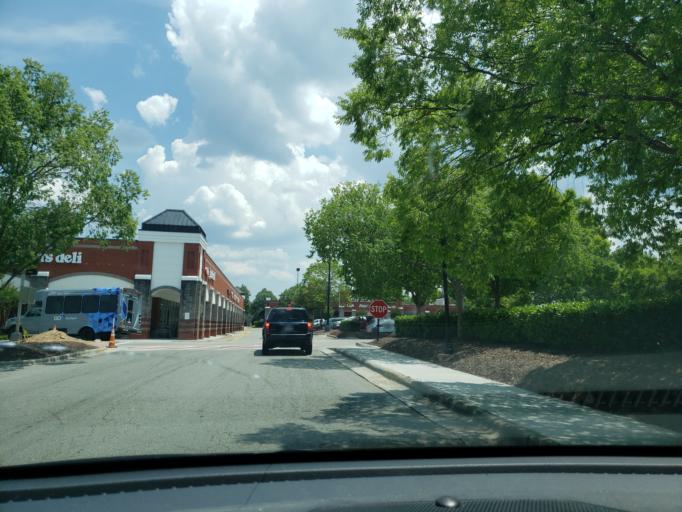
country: US
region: North Carolina
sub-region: Orange County
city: Chapel Hill
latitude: 35.9541
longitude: -78.9967
